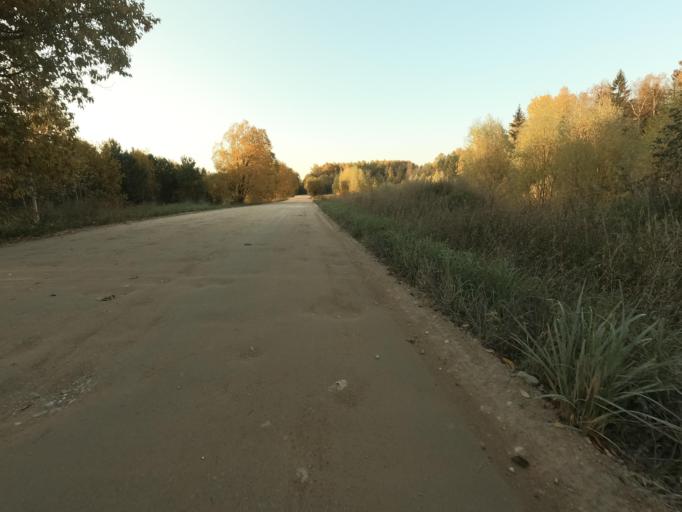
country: RU
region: Leningrad
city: Lyuban'
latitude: 59.0095
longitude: 31.0912
